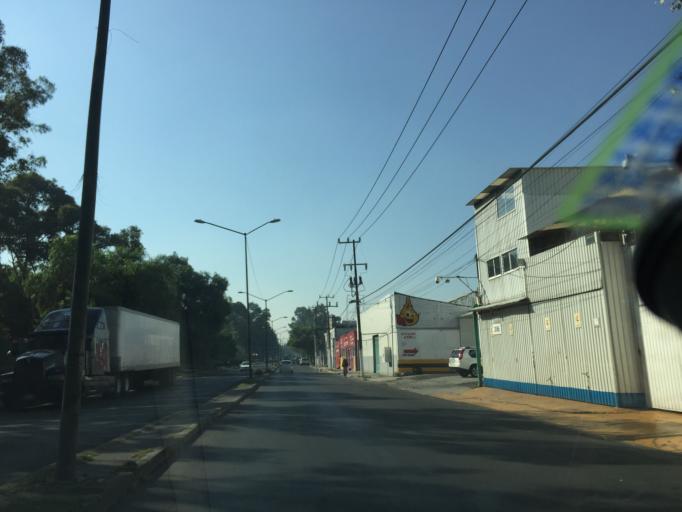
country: MX
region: Mexico
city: Vista Hermosa
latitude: 19.5008
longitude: -99.2128
